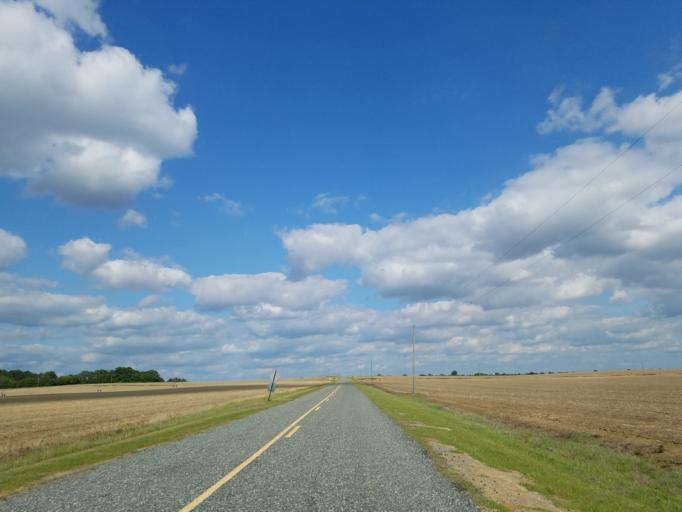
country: US
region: Georgia
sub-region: Dooly County
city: Unadilla
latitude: 32.2367
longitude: -83.7652
